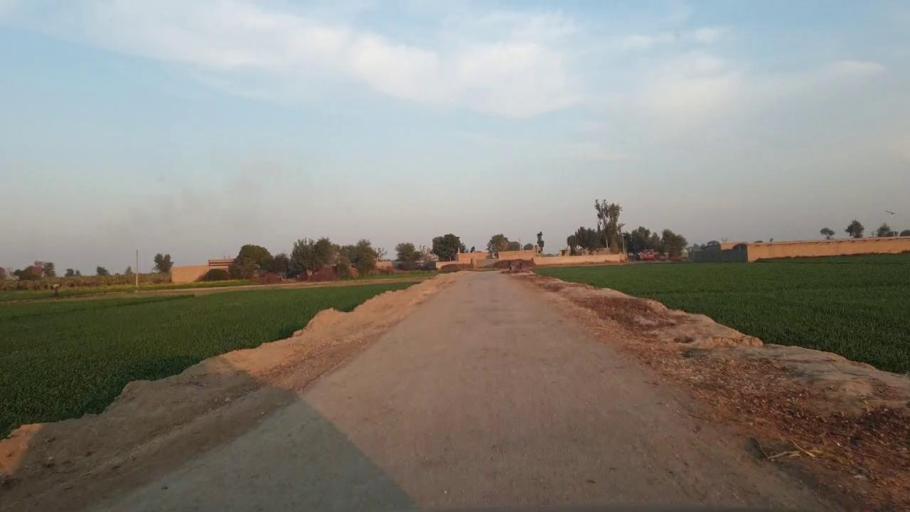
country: PK
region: Sindh
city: Shahpur Chakar
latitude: 26.1885
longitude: 68.6212
